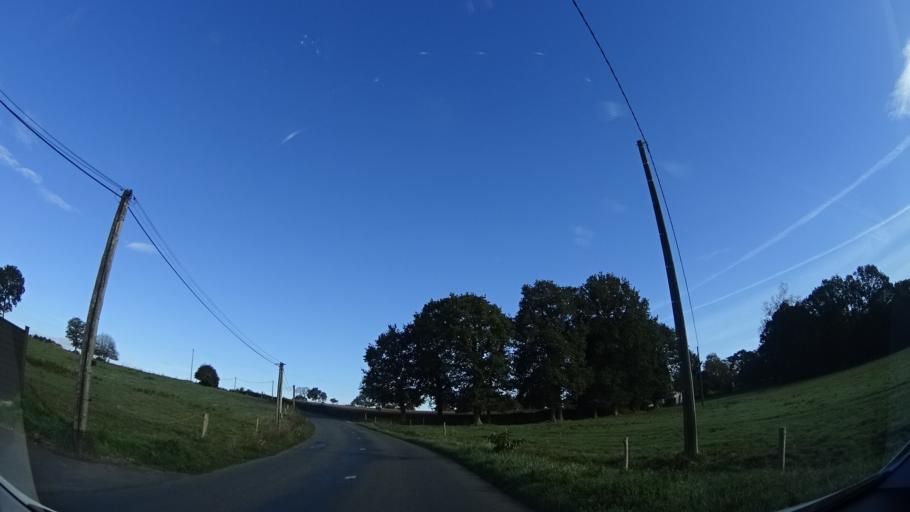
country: FR
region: Brittany
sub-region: Departement d'Ille-et-Vilaine
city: Geveze
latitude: 48.2006
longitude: -1.7910
